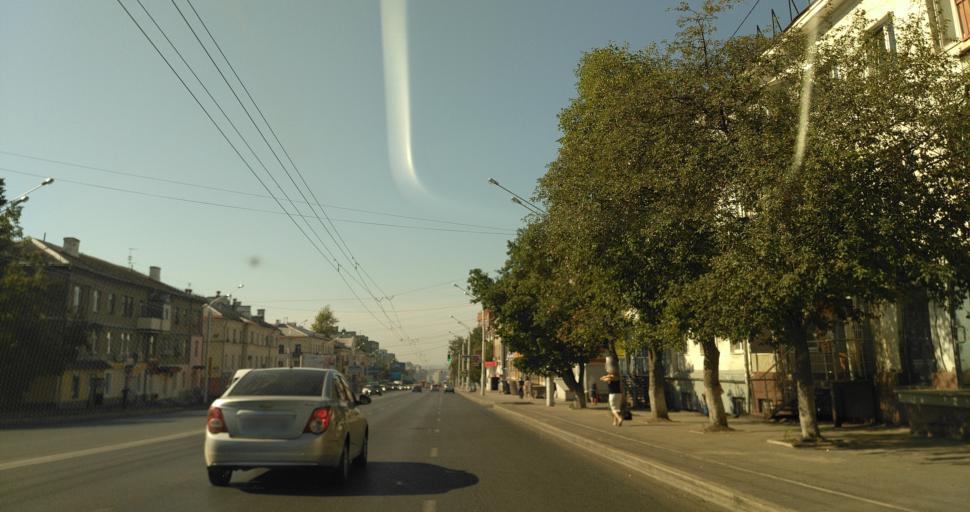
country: RU
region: Bashkortostan
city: Ufa
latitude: 54.7345
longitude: 55.9800
